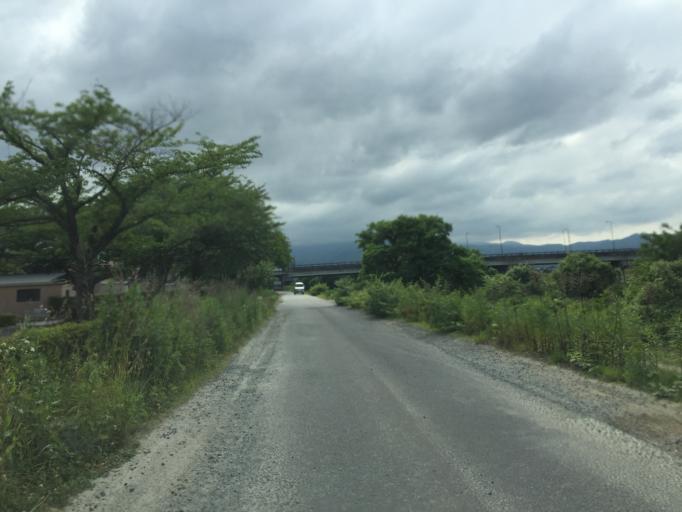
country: JP
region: Fukushima
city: Fukushima-shi
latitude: 37.7541
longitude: 140.4377
